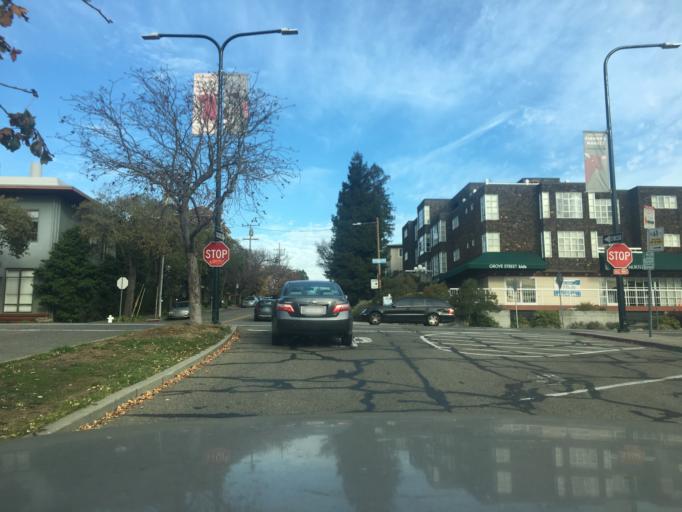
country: US
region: California
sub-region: Alameda County
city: Berkeley
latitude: 37.8818
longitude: -122.2694
